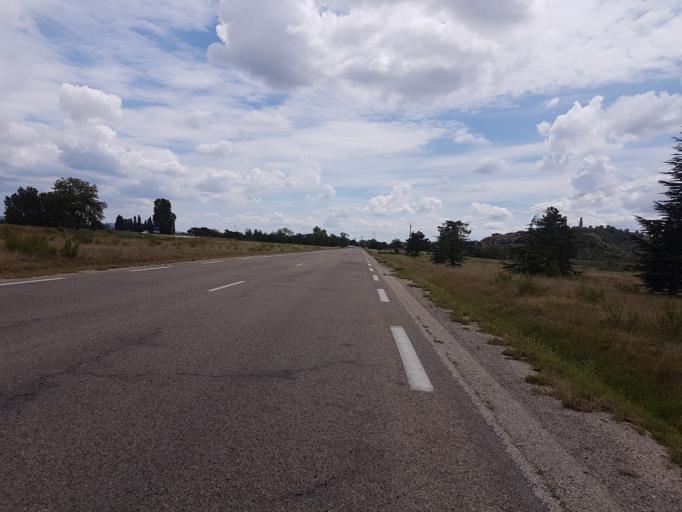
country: FR
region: Languedoc-Roussillon
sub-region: Departement du Gard
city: Vallabregues
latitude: 43.8495
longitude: 4.6186
